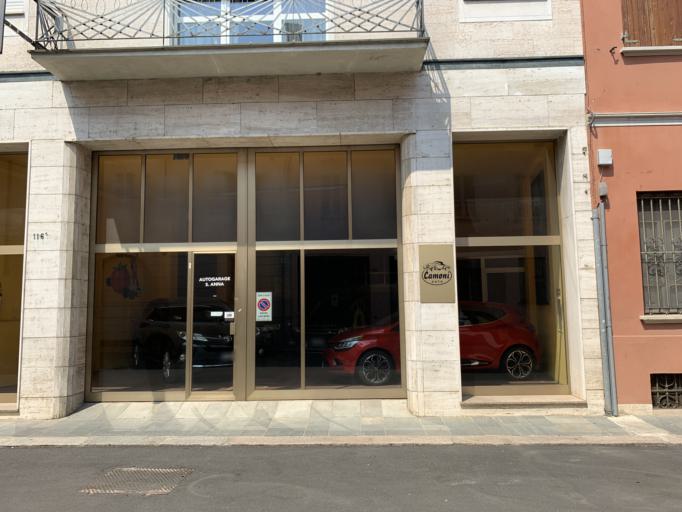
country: IT
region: Emilia-Romagna
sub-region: Provincia di Piacenza
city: Piacenza
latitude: 45.0476
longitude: 9.7036
